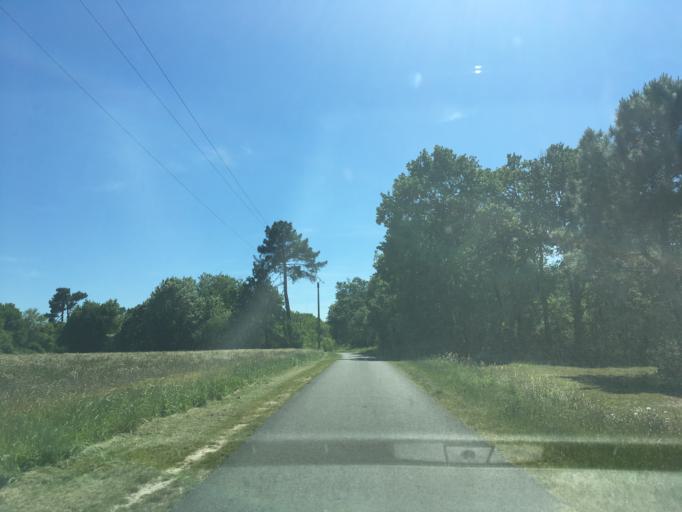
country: FR
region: Aquitaine
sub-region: Departement de la Gironde
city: Lesparre-Medoc
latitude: 45.3037
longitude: -0.8865
